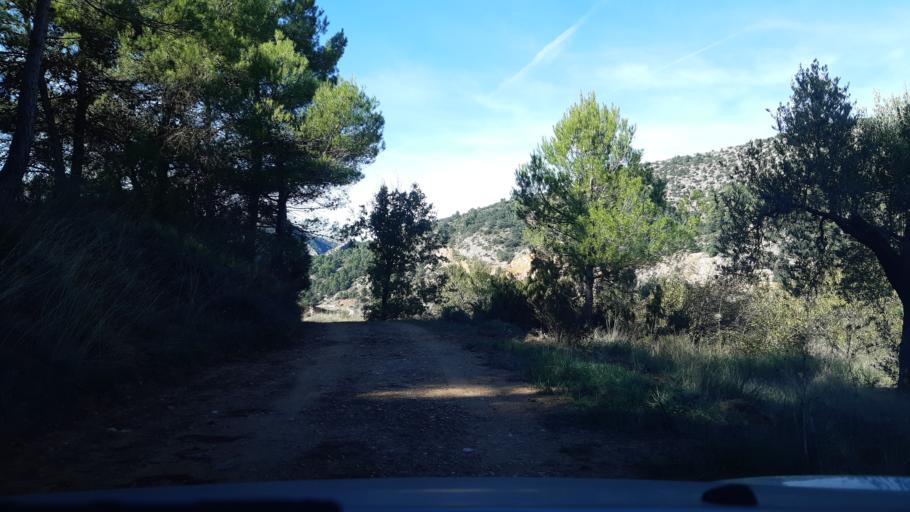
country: ES
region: Aragon
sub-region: Provincia de Teruel
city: Valderrobres
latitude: 40.8408
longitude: 0.2031
